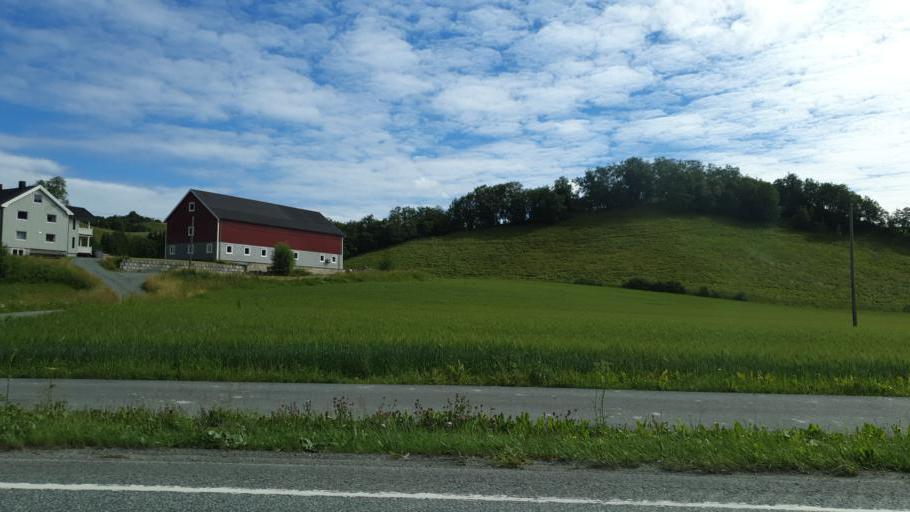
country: NO
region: Sor-Trondelag
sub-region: Melhus
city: Lundamo
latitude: 63.1847
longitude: 10.3141
